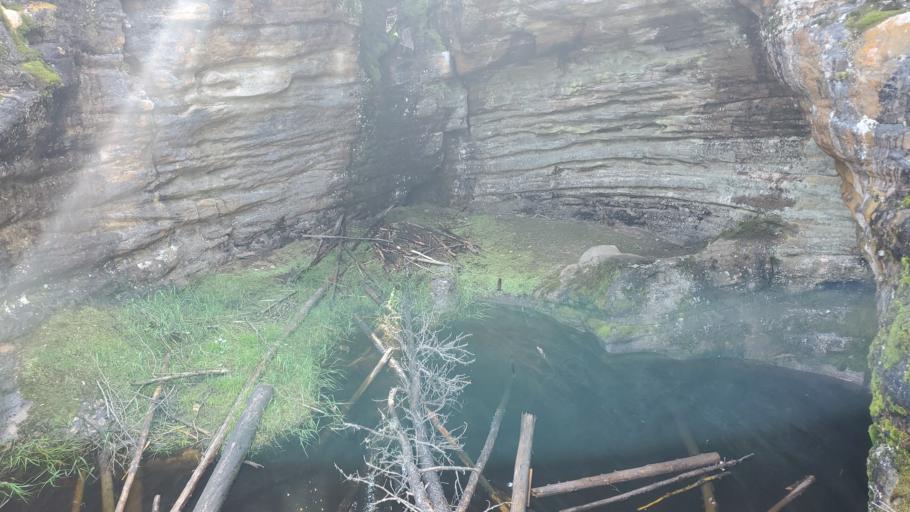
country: CA
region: Alberta
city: Jasper Park Lodge
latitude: 52.6645
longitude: -117.8858
